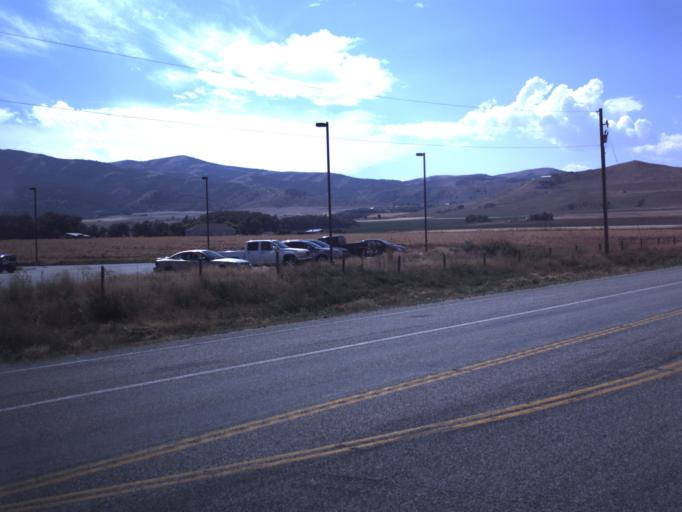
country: US
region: Utah
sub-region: Cache County
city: Mendon
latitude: 41.7517
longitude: -111.9833
